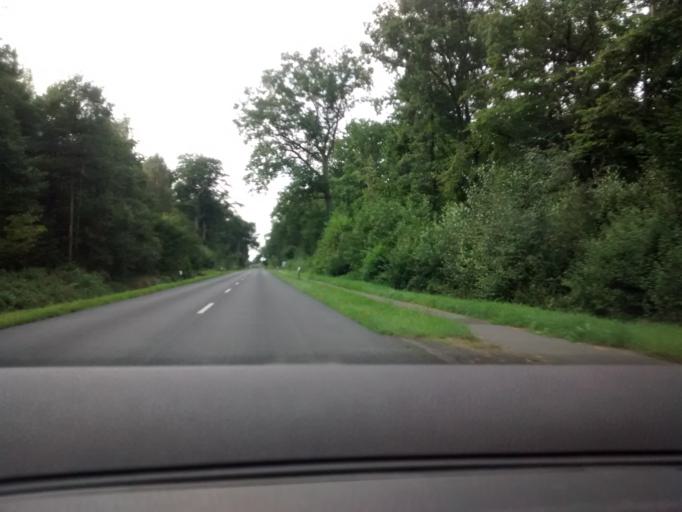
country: DE
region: Lower Saxony
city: Brietlingen
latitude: 53.3223
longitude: 10.4704
